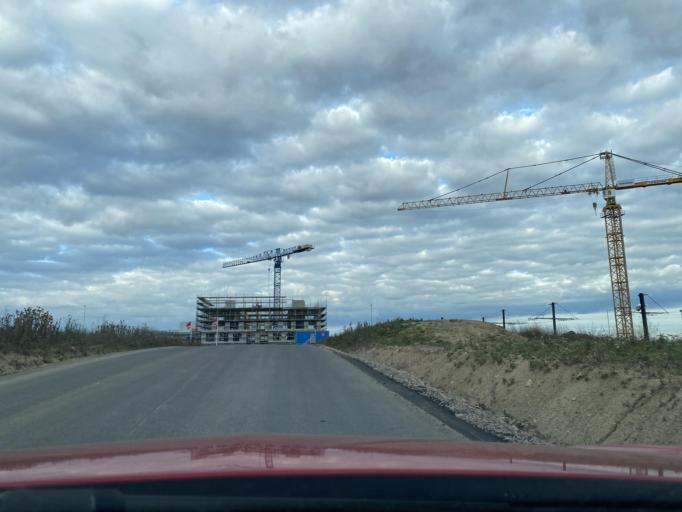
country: SE
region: Skane
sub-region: Lunds Kommun
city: Lund
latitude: 55.7301
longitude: 13.2410
